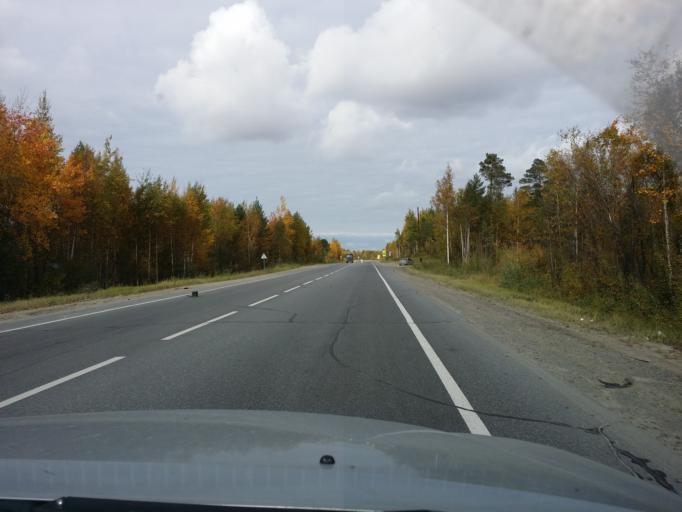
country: RU
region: Khanty-Mansiyskiy Avtonomnyy Okrug
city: Megion
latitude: 61.1058
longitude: 76.0435
